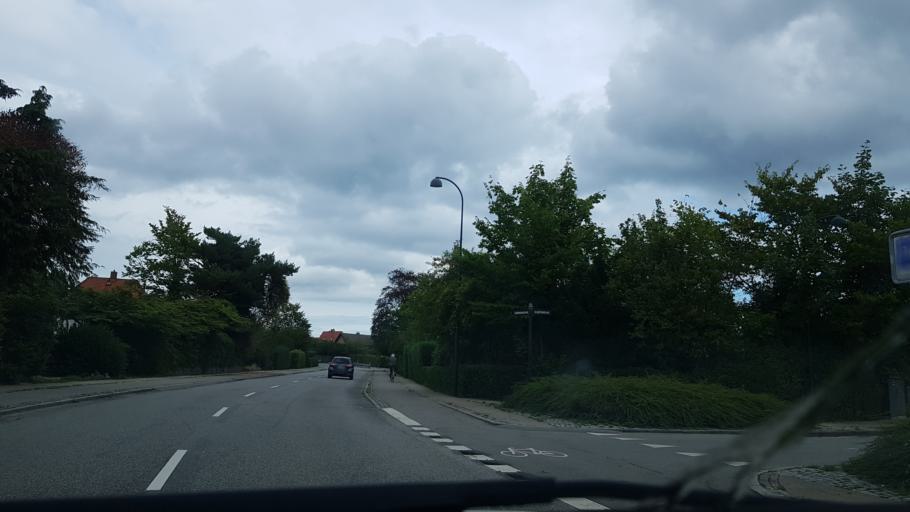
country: DK
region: Capital Region
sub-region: Gentofte Kommune
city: Charlottenlund
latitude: 55.7581
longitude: 12.5806
